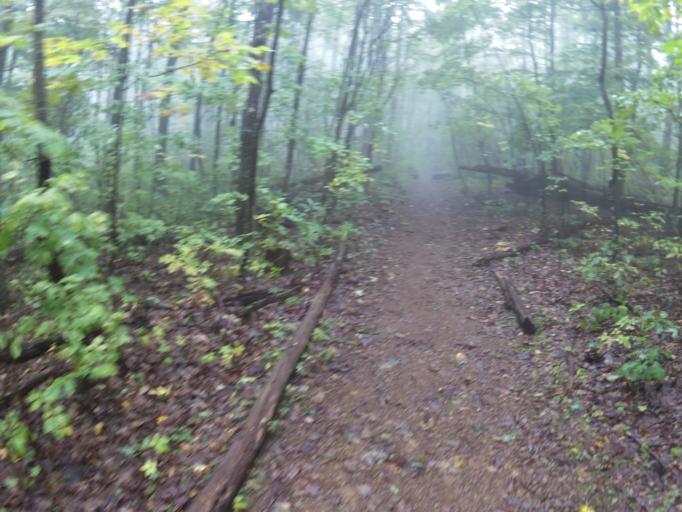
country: US
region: Virginia
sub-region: Rappahannock County
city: Washington
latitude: 38.7810
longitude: -78.2893
